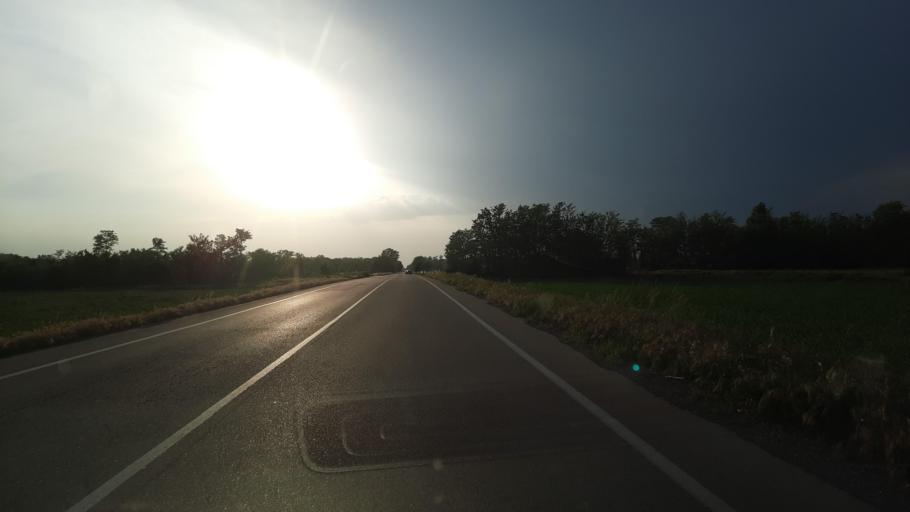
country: IT
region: Lombardy
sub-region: Provincia di Pavia
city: Cergnago
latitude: 45.2302
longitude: 8.8141
